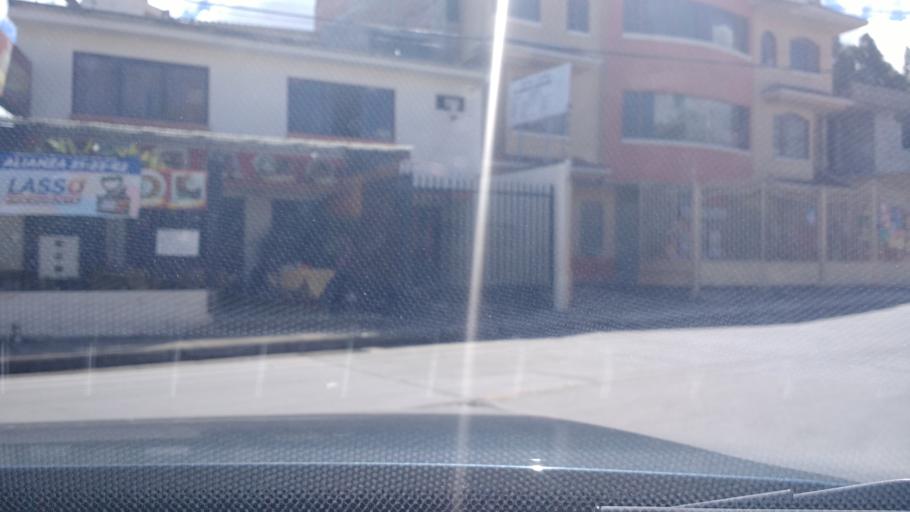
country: EC
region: Azuay
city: Cuenca
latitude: -2.9025
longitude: -79.0327
